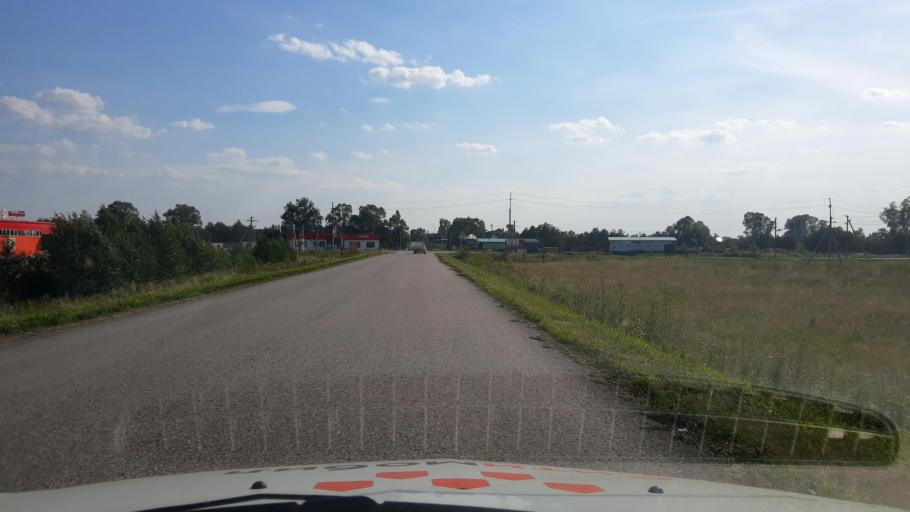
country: RU
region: Bashkortostan
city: Kabakovo
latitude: 54.6621
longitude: 56.2030
